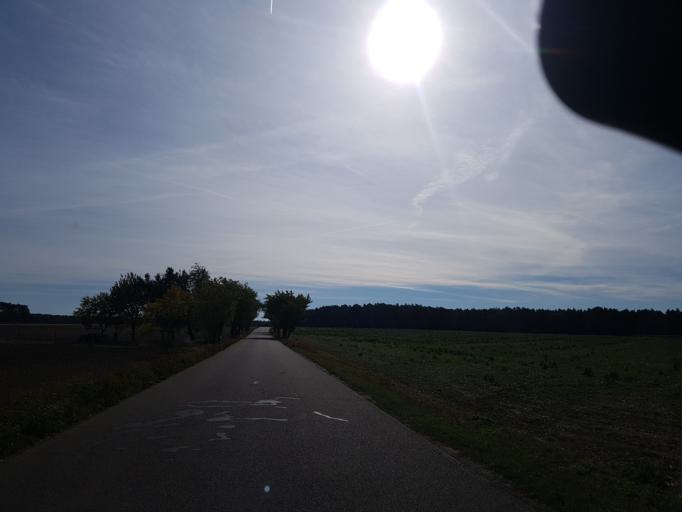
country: DE
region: Brandenburg
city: Schlieben
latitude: 51.7764
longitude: 13.3258
